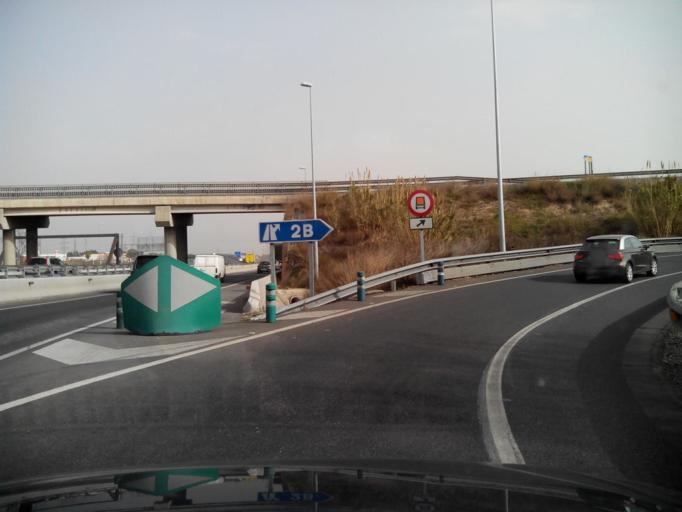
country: ES
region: Catalonia
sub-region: Provincia de Tarragona
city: Tarragona
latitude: 41.1298
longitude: 1.2288
